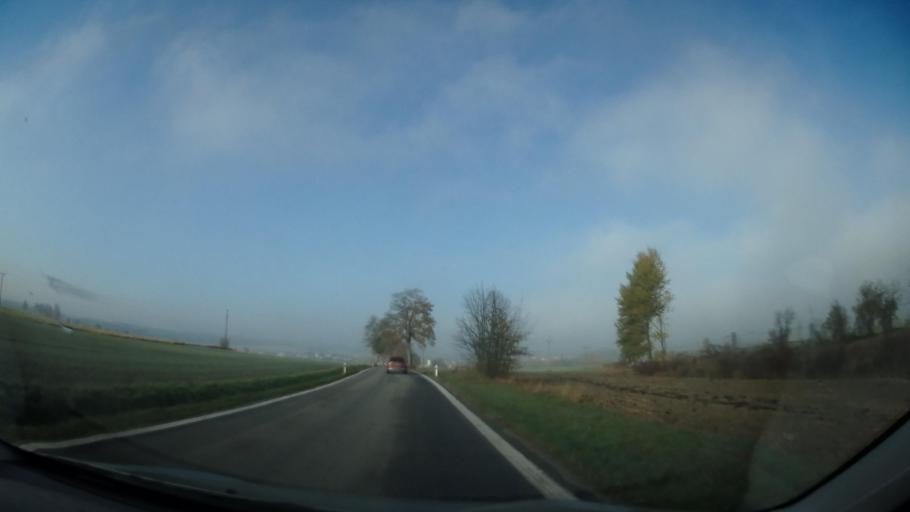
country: CZ
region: Vysocina
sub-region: Okres Zd'ar nad Sazavou
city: Zd'ar nad Sazavou
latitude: 49.4860
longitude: 16.0042
